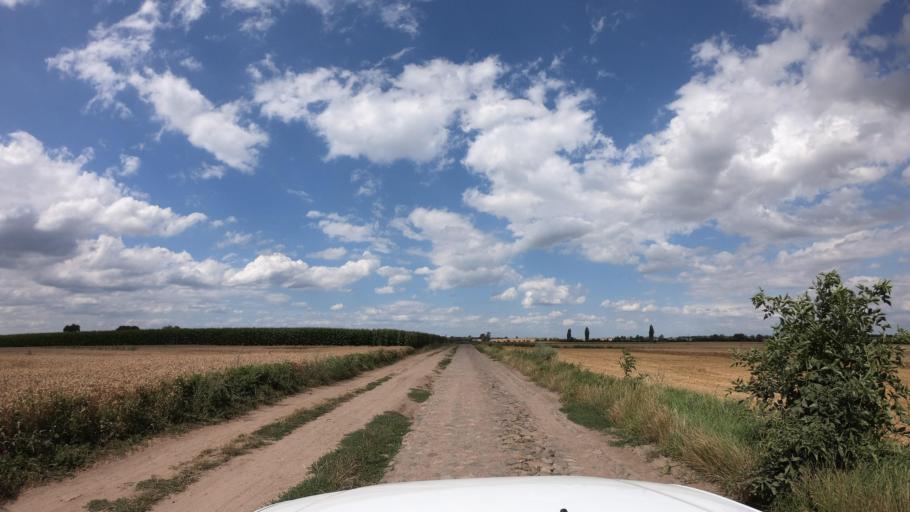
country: PL
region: West Pomeranian Voivodeship
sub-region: Powiat pyrzycki
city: Warnice
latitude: 53.2440
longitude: 14.9129
